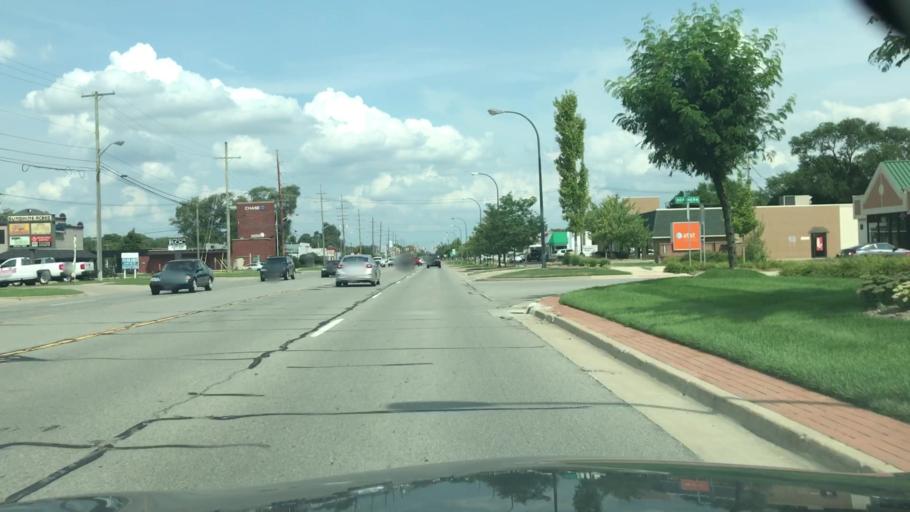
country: US
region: Michigan
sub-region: Wayne County
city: Plymouth
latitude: 42.3586
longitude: -83.4736
